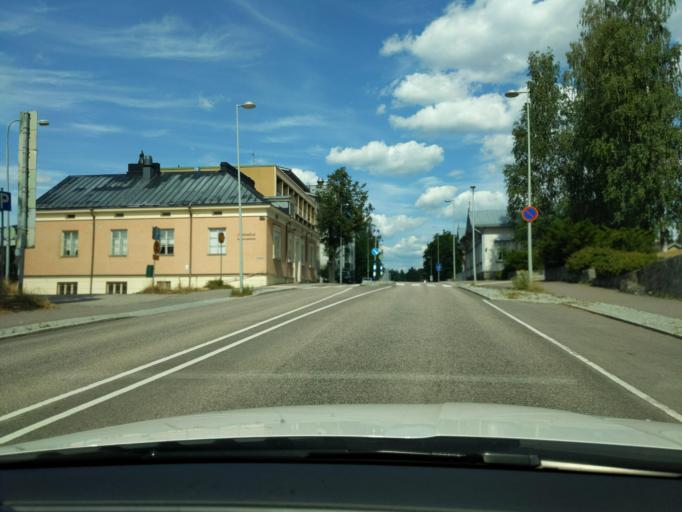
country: FI
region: Paijanne Tavastia
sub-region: Lahti
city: Heinola
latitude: 61.2018
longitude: 26.0362
